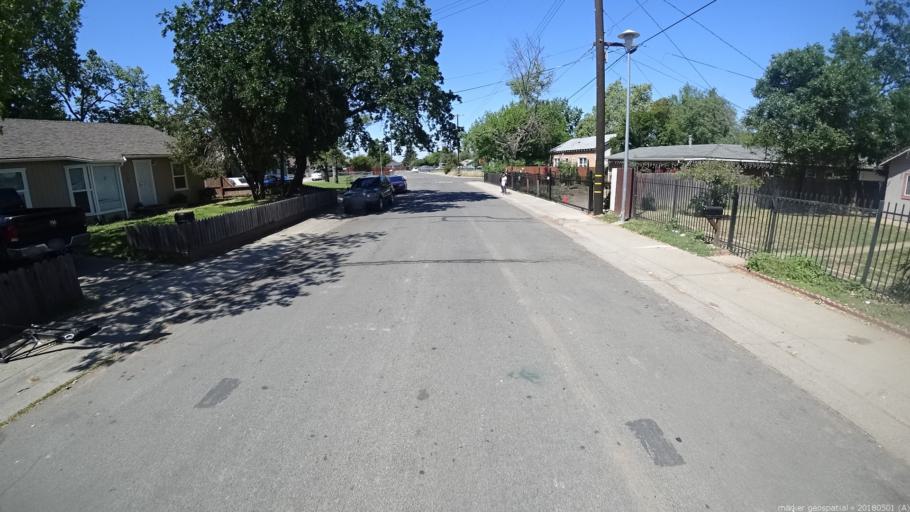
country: US
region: California
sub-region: Sacramento County
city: Rio Linda
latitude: 38.6311
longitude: -121.4411
